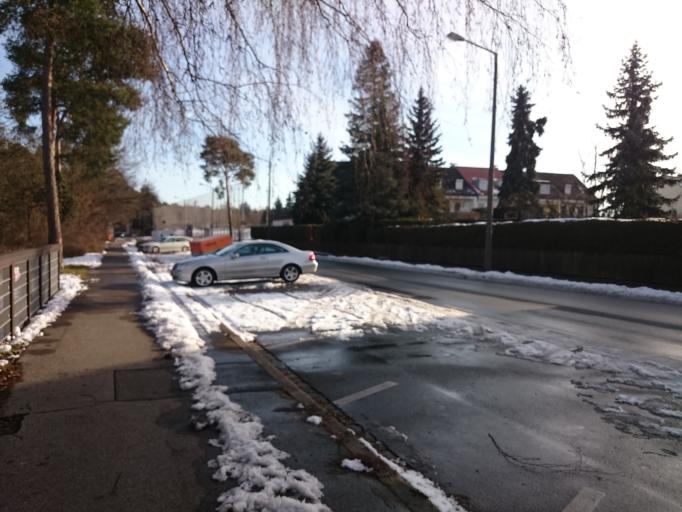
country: DE
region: Bavaria
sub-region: Regierungsbezirk Mittelfranken
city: Nuernberg
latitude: 49.4385
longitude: 11.1301
